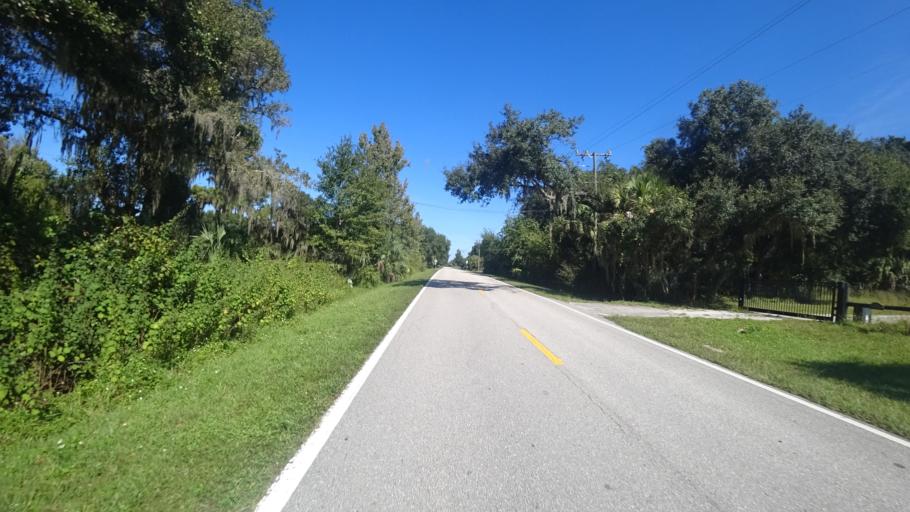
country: US
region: Florida
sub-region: Sarasota County
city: Lake Sarasota
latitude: 27.3076
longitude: -82.2671
